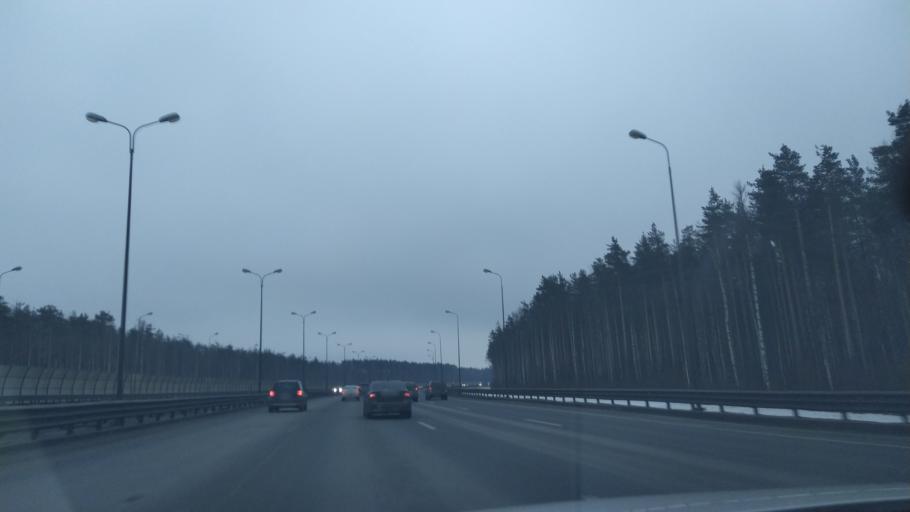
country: RU
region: St.-Petersburg
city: Krasnogvargeisky
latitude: 59.9740
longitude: 30.5416
